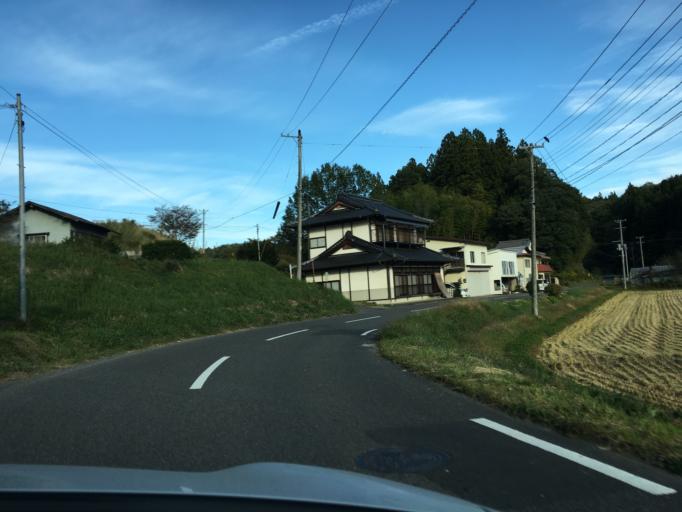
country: JP
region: Fukushima
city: Ishikawa
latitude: 37.1853
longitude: 140.5558
